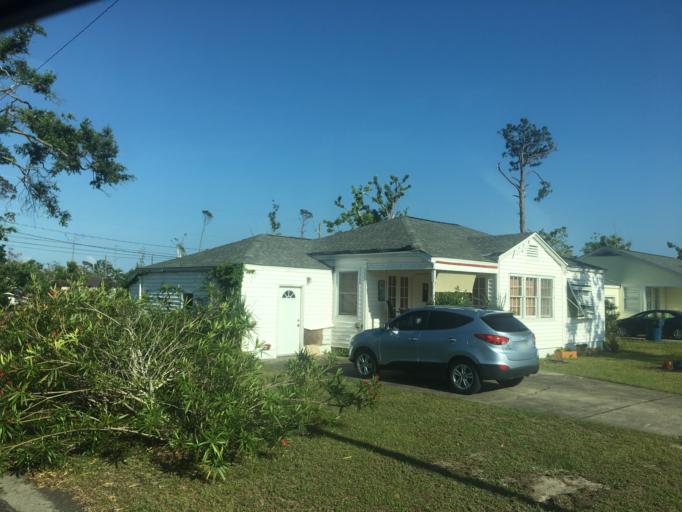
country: US
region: Florida
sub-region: Bay County
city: Panama City
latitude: 30.1495
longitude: -85.6503
